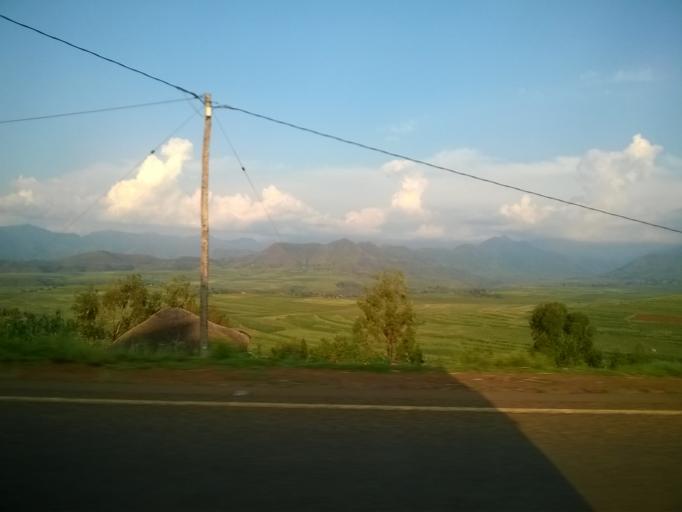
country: LS
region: Leribe
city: Leribe
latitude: -29.0140
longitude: 28.2182
